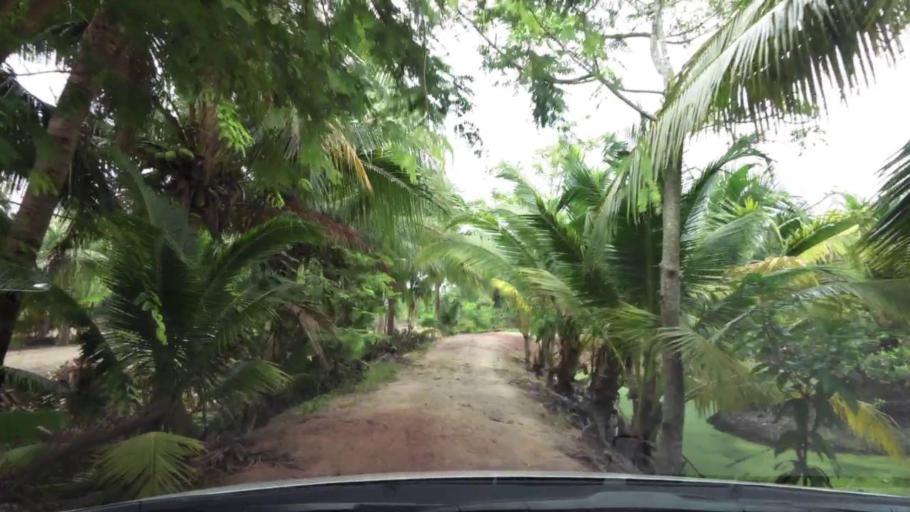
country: TH
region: Ratchaburi
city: Damnoen Saduak
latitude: 13.5608
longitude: 100.0047
